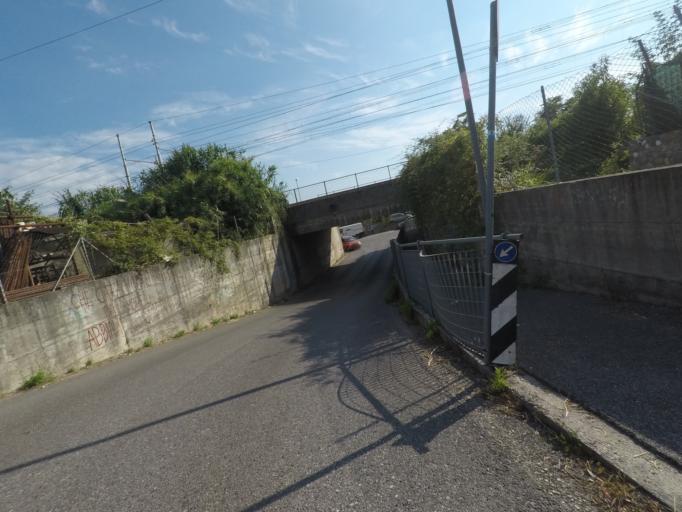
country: IT
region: Tuscany
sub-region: Provincia di Massa-Carrara
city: Capanne-Prato-Cinquale
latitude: 44.0174
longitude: 10.1453
